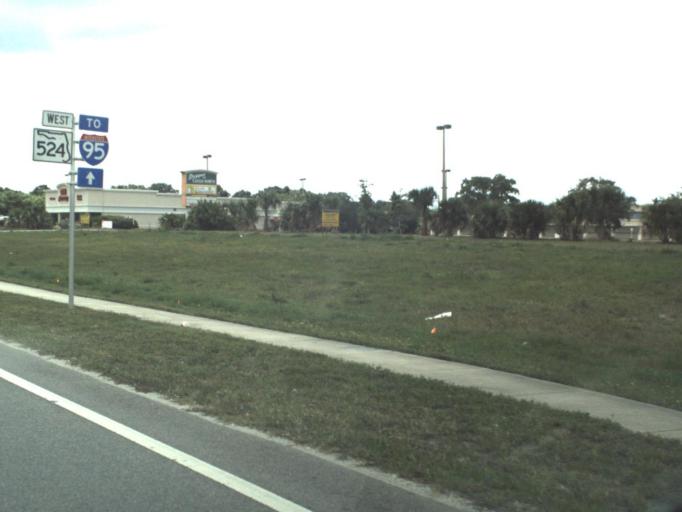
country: US
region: Florida
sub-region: Brevard County
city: Cocoa
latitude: 28.3969
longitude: -80.7647
